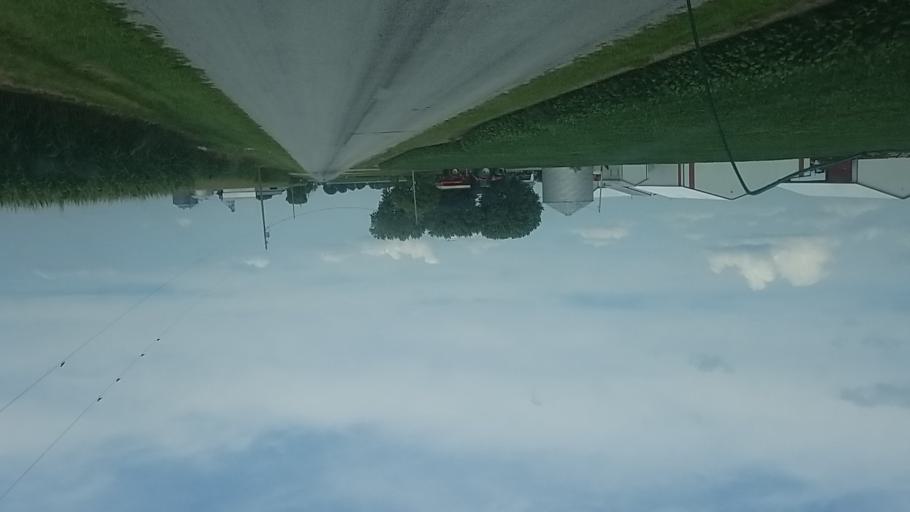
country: US
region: Ohio
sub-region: Wyandot County
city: Upper Sandusky
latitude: 40.8179
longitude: -83.3312
